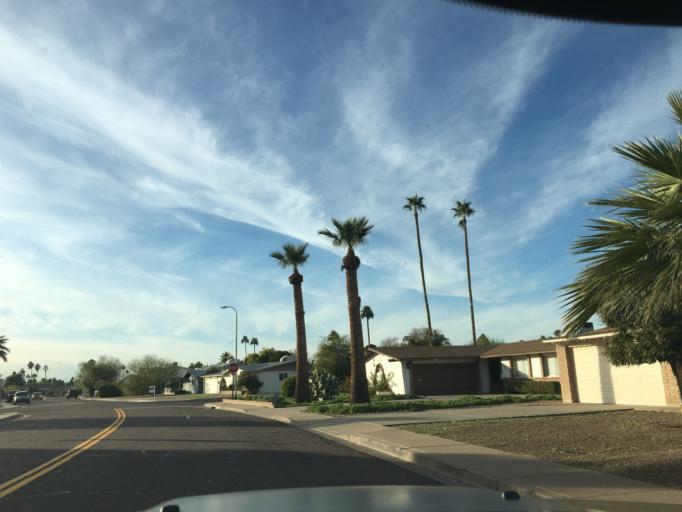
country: US
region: Arizona
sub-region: Maricopa County
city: Tempe
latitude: 33.3690
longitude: -111.9068
